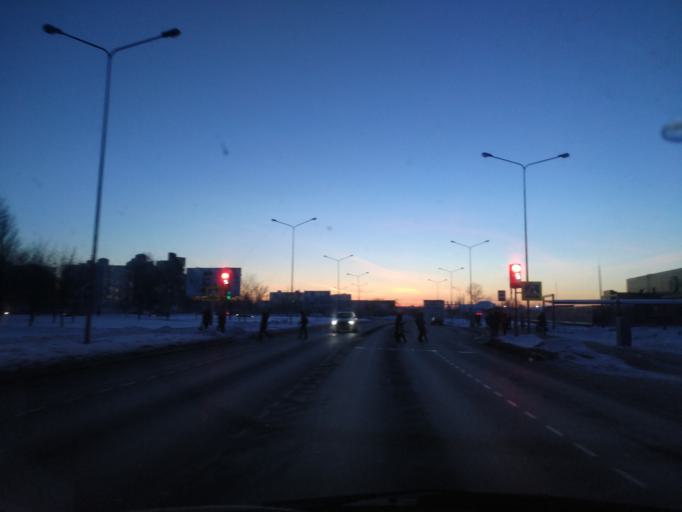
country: BY
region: Mogilev
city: Mahilyow
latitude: 53.8797
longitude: 30.3184
